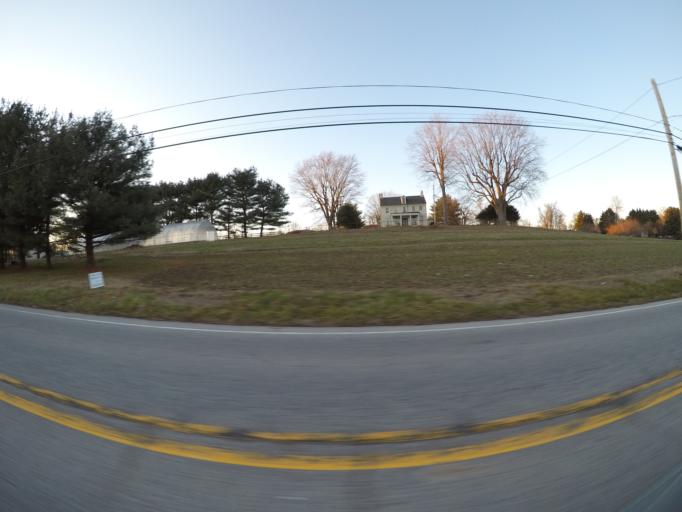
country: US
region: Maryland
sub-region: Cecil County
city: Rising Sun
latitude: 39.6747
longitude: -76.1648
